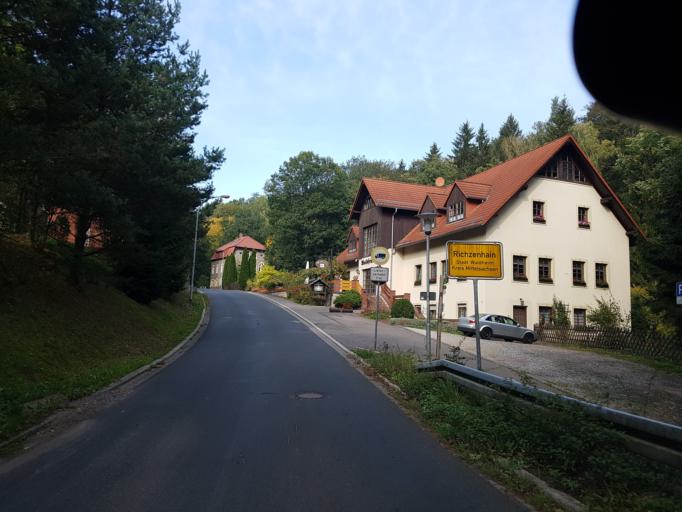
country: DE
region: Saxony
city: Waldheim
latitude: 51.0818
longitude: 13.0123
